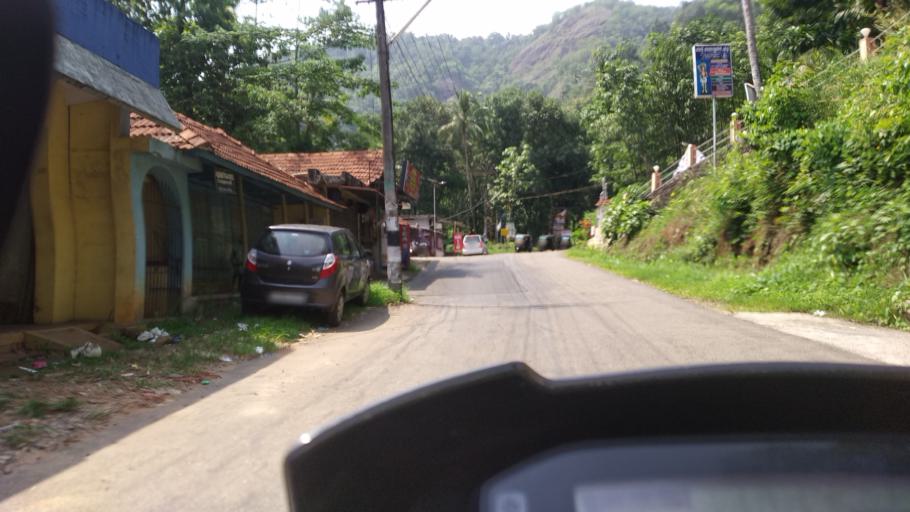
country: IN
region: Kerala
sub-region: Kottayam
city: Erattupetta
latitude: 9.6910
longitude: 76.8444
